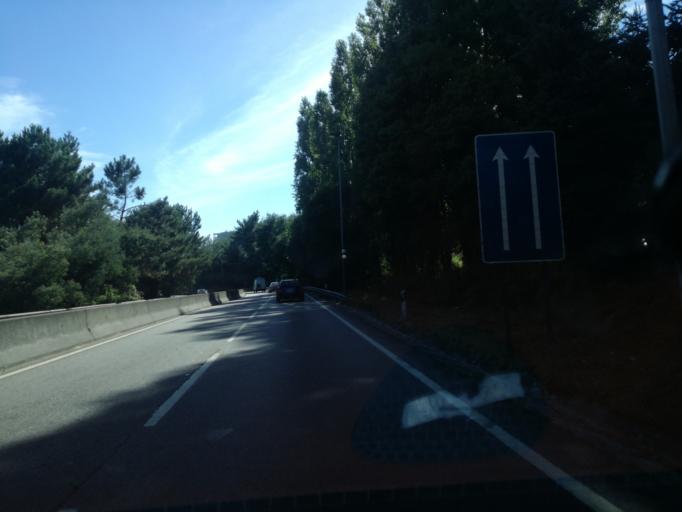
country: PT
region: Braga
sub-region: Guimaraes
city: Guimaraes
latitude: 41.4541
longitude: -8.2955
